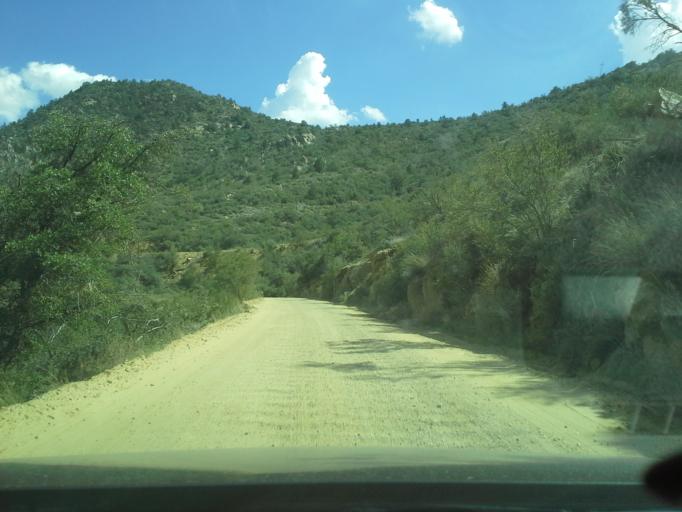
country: US
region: Arizona
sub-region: Yavapai County
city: Mayer
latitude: 34.2485
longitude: -112.2960
